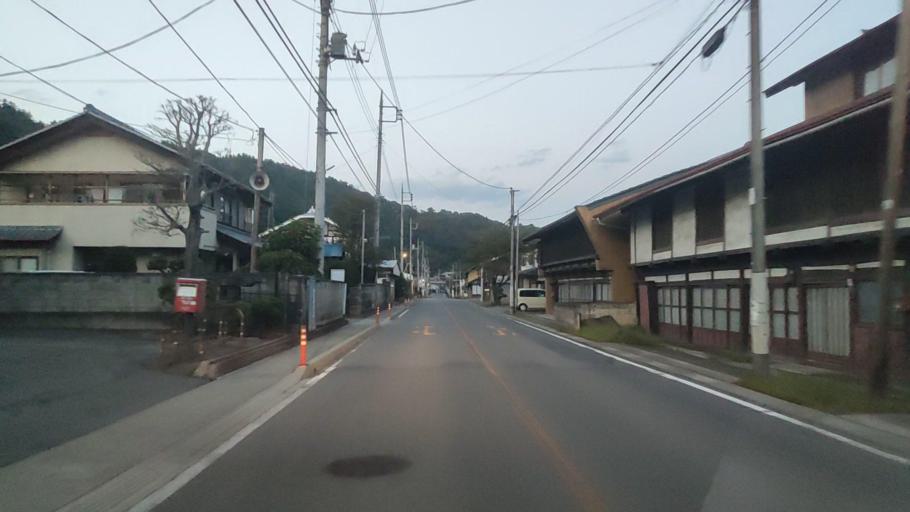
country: JP
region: Gunma
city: Nakanojomachi
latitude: 36.5501
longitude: 138.6067
